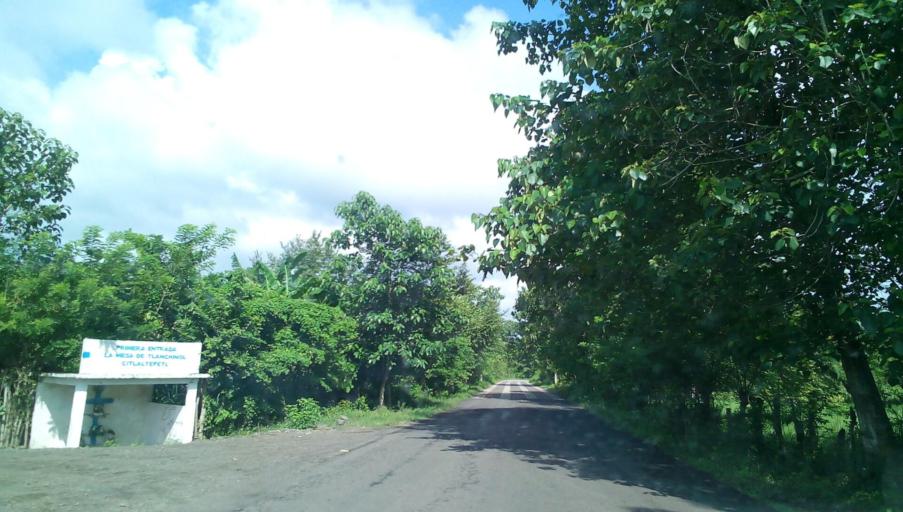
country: MX
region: Veracruz
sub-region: Citlaltepetl
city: Las Sabinas
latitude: 21.3470
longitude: -97.8926
